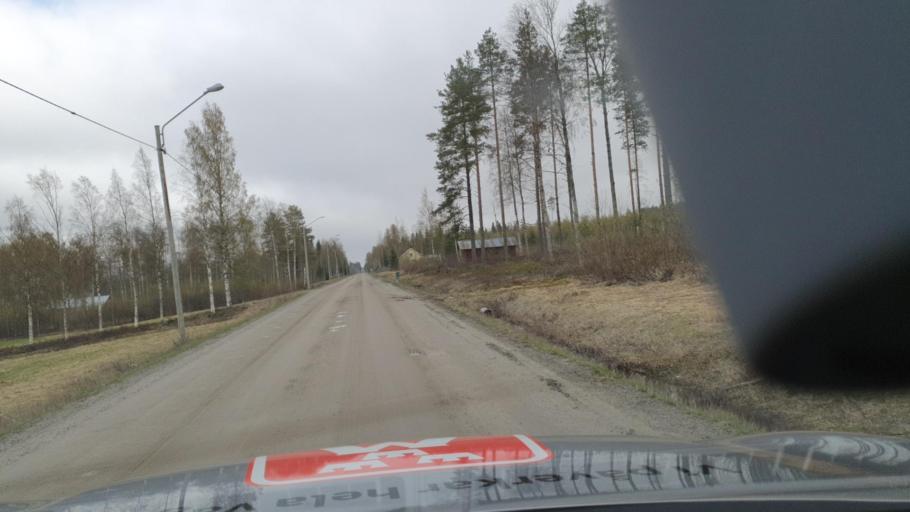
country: SE
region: Vaesterbotten
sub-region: Bjurholms Kommun
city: Bjurholm
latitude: 63.6576
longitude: 19.0332
